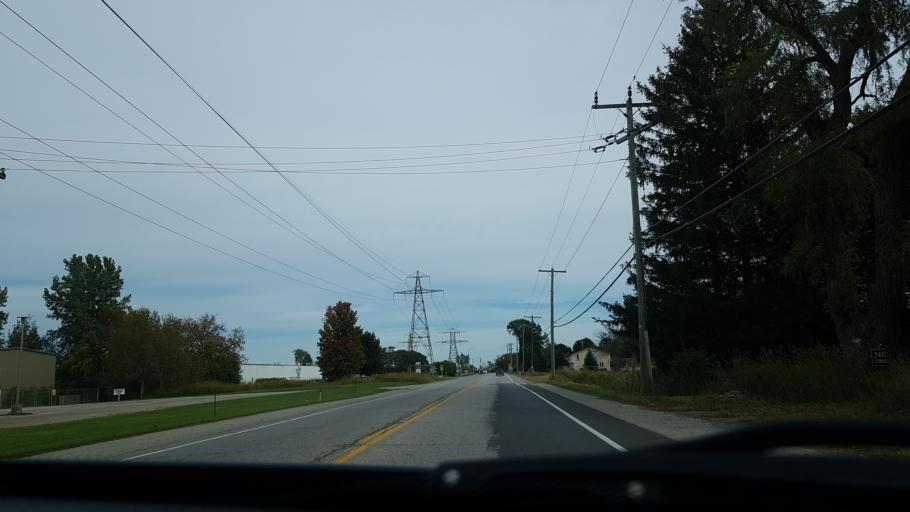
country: CA
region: Ontario
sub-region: Wellington County
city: Guelph
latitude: 43.5023
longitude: -80.2705
